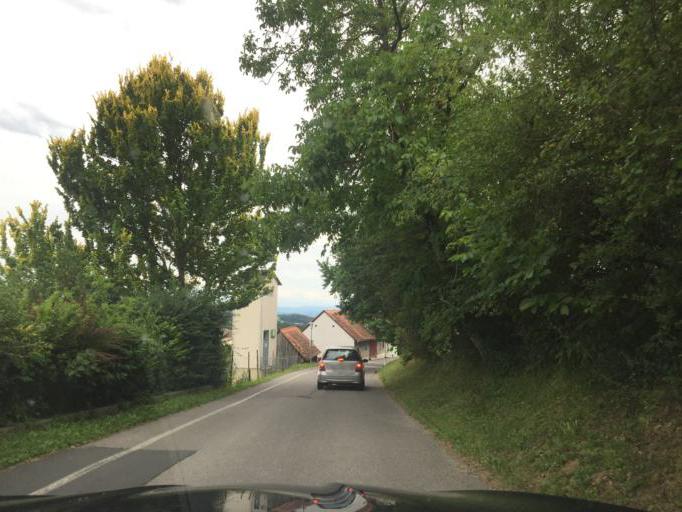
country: AT
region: Styria
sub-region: Politischer Bezirk Graz-Umgebung
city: Hart bei Graz
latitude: 47.0608
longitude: 15.5149
